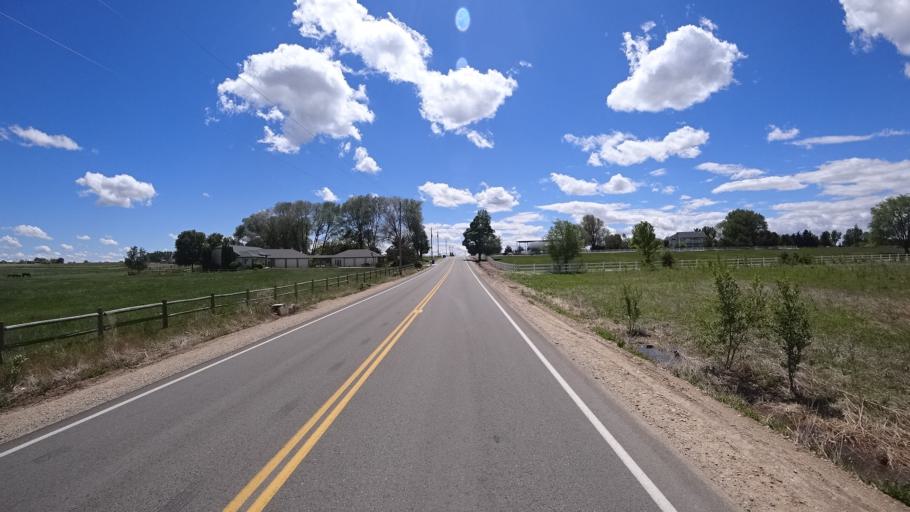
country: US
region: Idaho
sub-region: Ada County
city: Meridian
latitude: 43.5737
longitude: -116.4537
